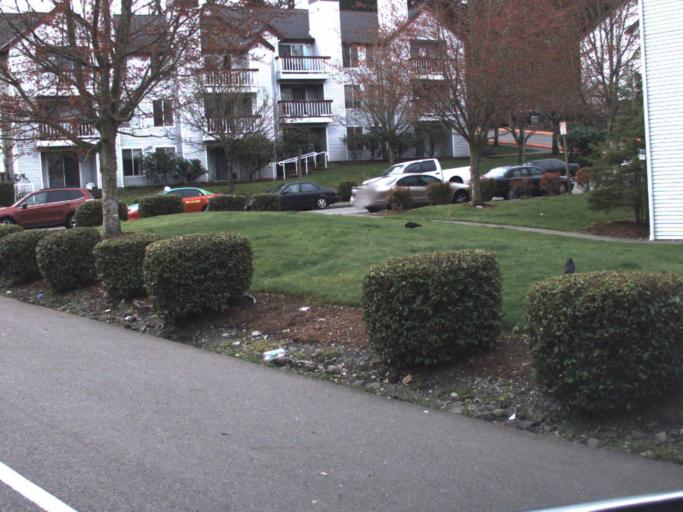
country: US
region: Washington
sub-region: King County
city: Normandy Park
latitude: 47.4451
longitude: -122.3295
